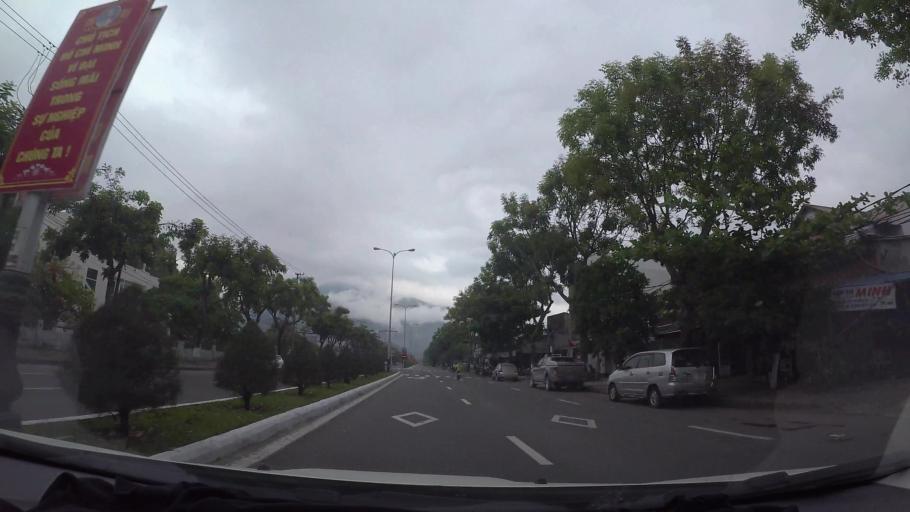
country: VN
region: Da Nang
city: Lien Chieu
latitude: 16.1306
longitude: 108.1195
